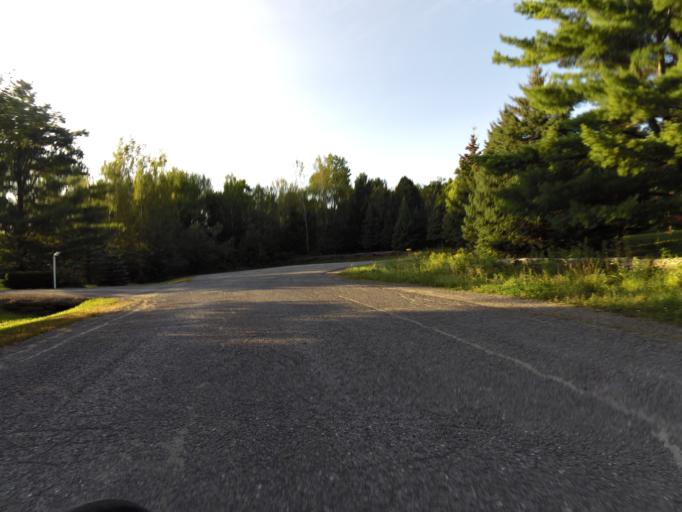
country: CA
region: Ontario
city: Bells Corners
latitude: 45.3802
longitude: -75.9563
